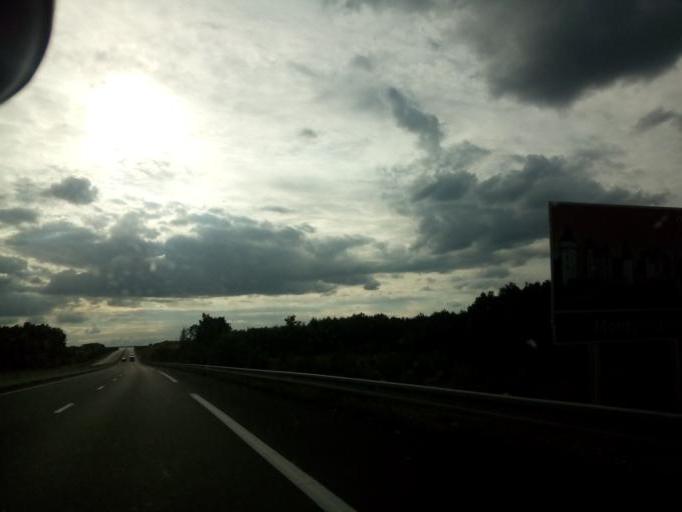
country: FR
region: Centre
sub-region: Departement du Loir-et-Cher
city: Saint-Georges-sur-Cher
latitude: 47.2951
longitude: 1.1464
